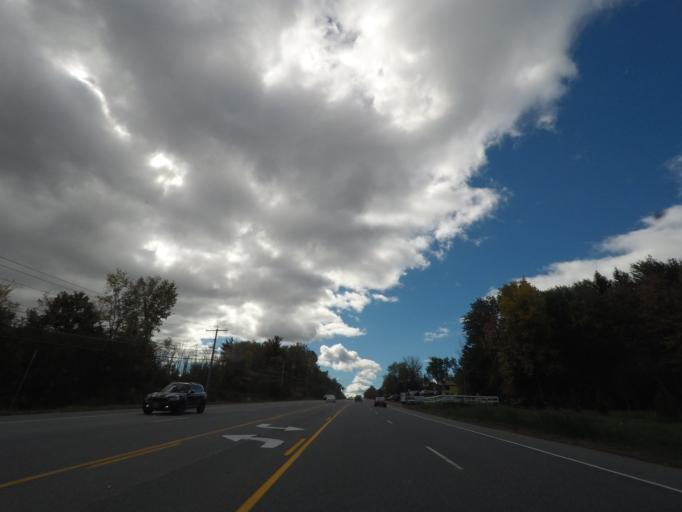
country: US
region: New York
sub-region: Albany County
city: Cohoes
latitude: 42.8124
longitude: -73.7318
